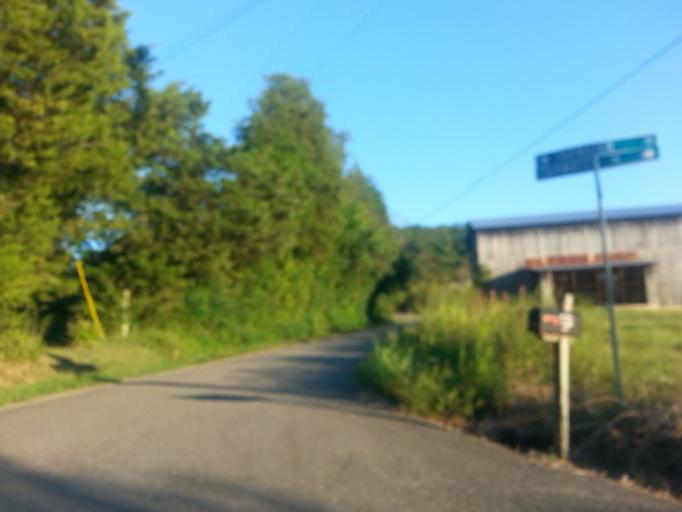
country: US
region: Tennessee
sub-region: Blount County
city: Wildwood
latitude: 35.8874
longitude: -83.8641
